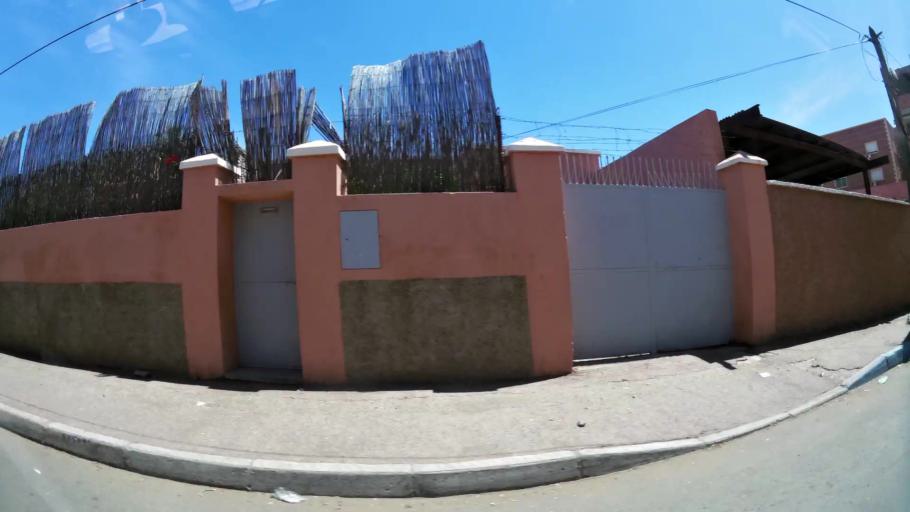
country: MA
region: Marrakech-Tensift-Al Haouz
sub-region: Marrakech
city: Marrakesh
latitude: 31.6285
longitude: -8.0423
